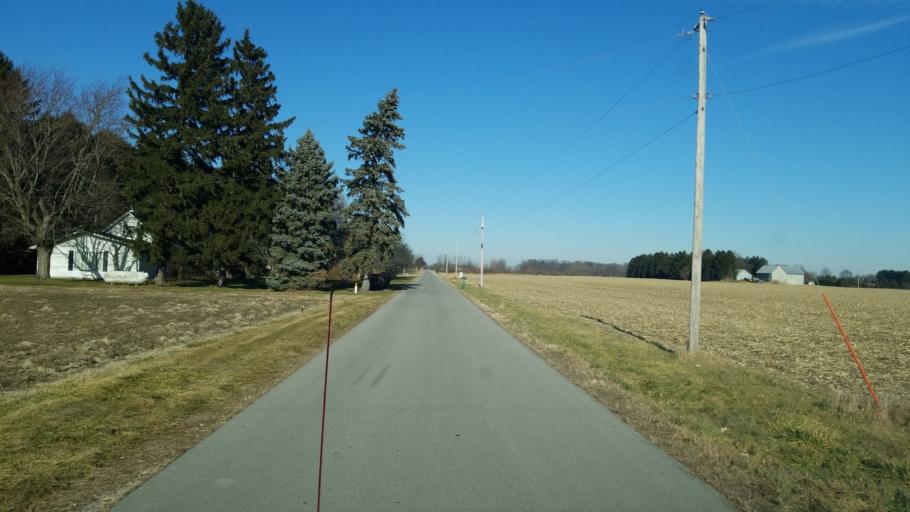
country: US
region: Ohio
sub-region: Henry County
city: Liberty Center
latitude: 41.3787
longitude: -83.9706
